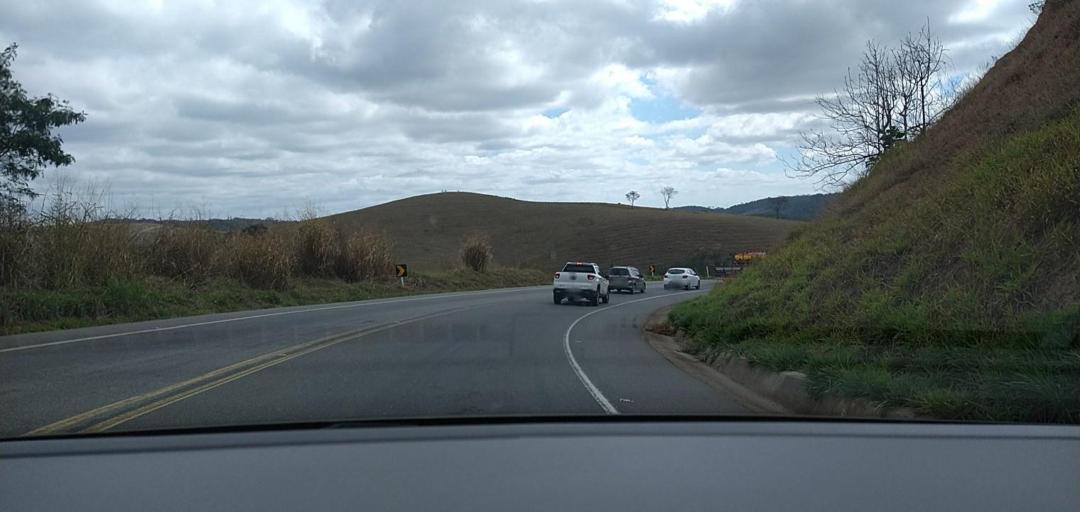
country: BR
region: Minas Gerais
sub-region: Ponte Nova
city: Ponte Nova
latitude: -20.5296
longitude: -42.8953
